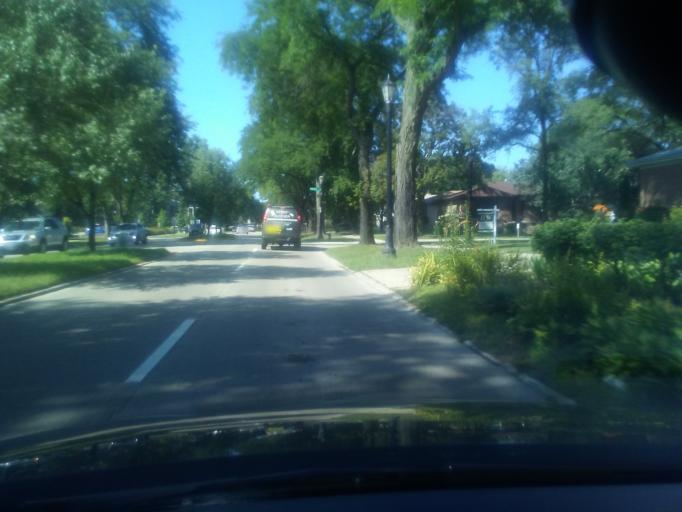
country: US
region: Illinois
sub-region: Cook County
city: Wilmette
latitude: 42.0612
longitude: -87.7273
